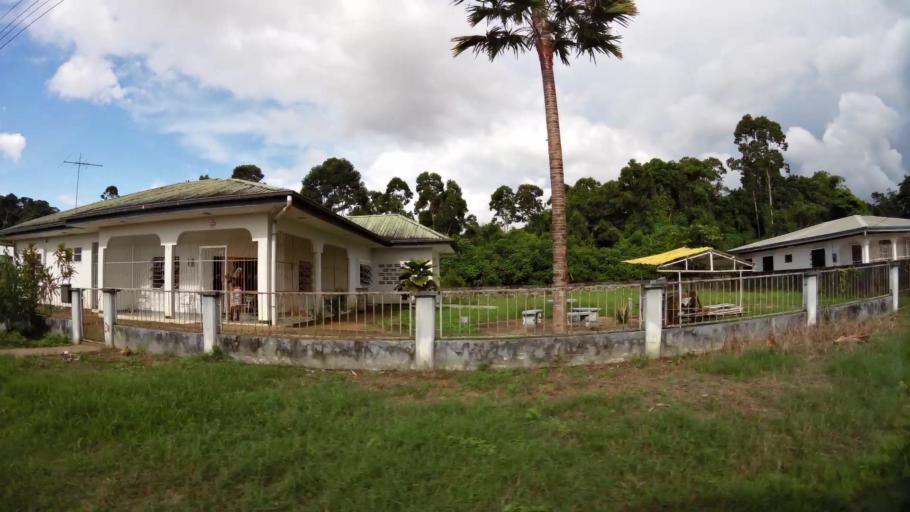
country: SR
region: Paramaribo
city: Paramaribo
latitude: 5.8554
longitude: -55.1775
